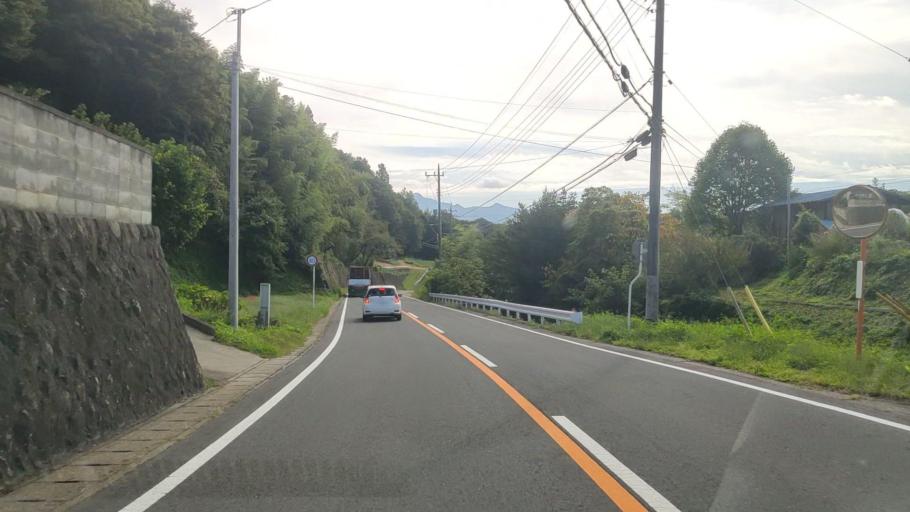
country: JP
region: Gunma
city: Numata
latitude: 36.6256
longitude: 139.0208
